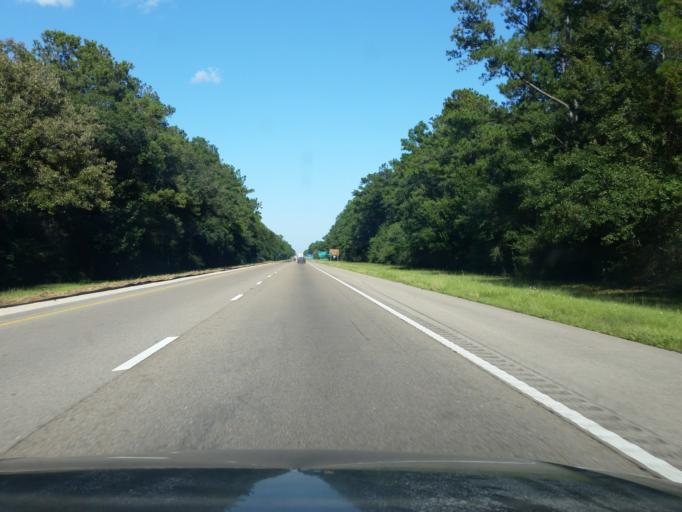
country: US
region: Mississippi
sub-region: Hancock County
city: Pearlington
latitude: 30.3107
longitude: -89.6133
